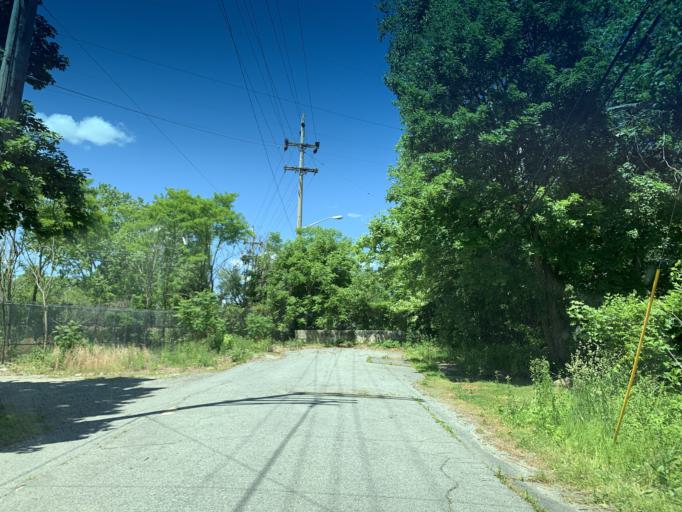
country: US
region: Maryland
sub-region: Cecil County
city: North East
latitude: 39.6048
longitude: -75.9435
